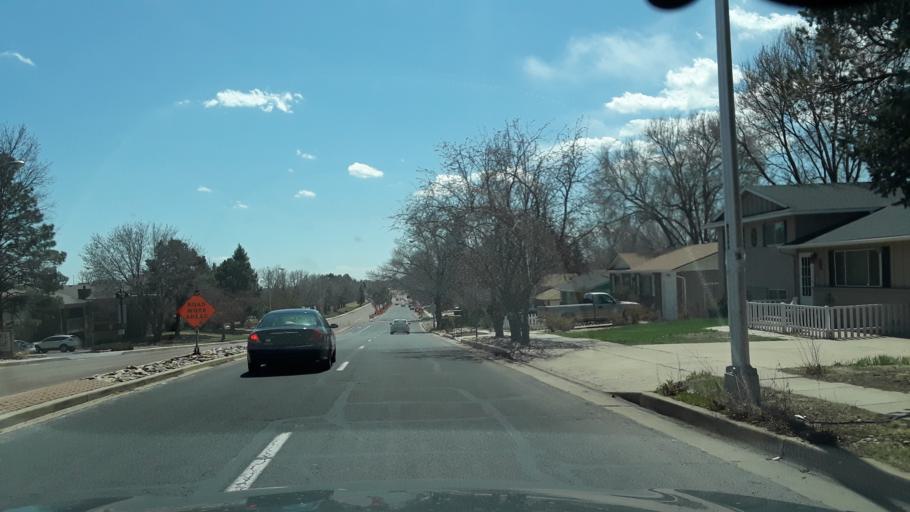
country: US
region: Colorado
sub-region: El Paso County
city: Colorado Springs
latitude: 38.8468
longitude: -104.7667
